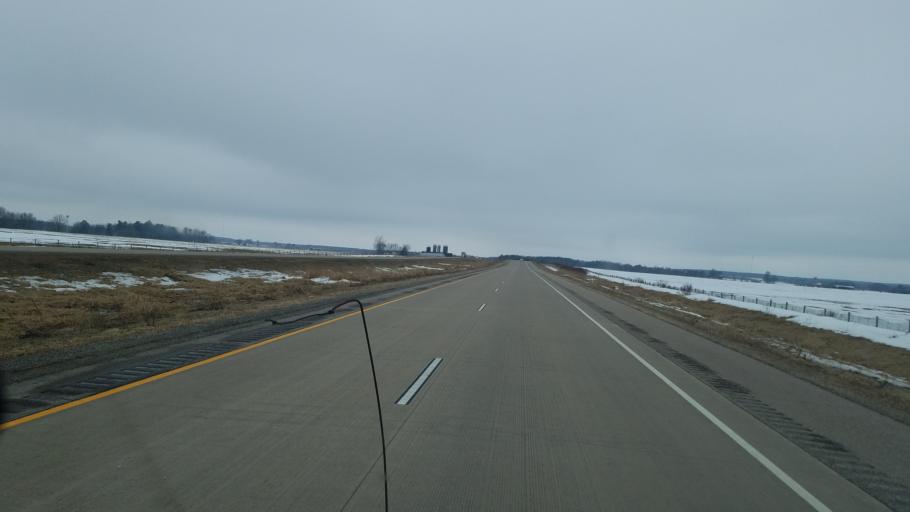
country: US
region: Wisconsin
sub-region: Marathon County
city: Stratford
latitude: 44.6207
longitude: -89.9037
